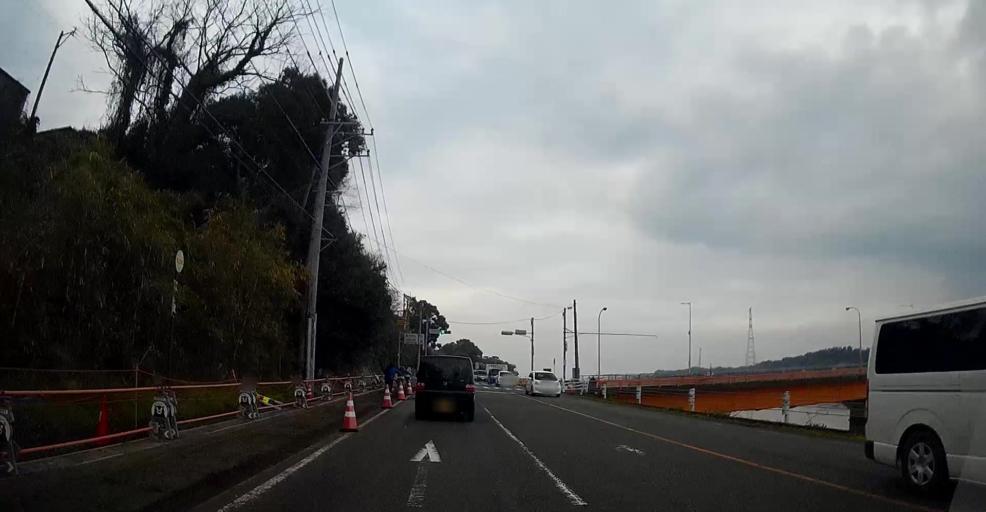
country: JP
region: Kumamoto
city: Yatsushiro
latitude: 32.6125
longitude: 130.4929
